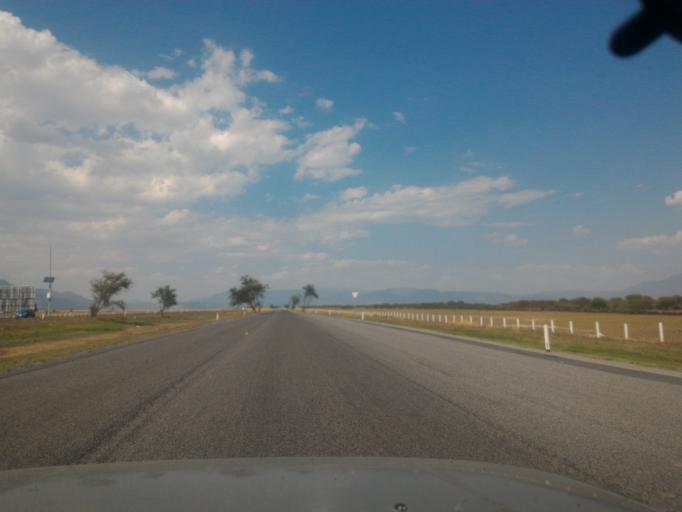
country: MX
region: Jalisco
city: Atoyac
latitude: 20.0176
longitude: -103.5317
